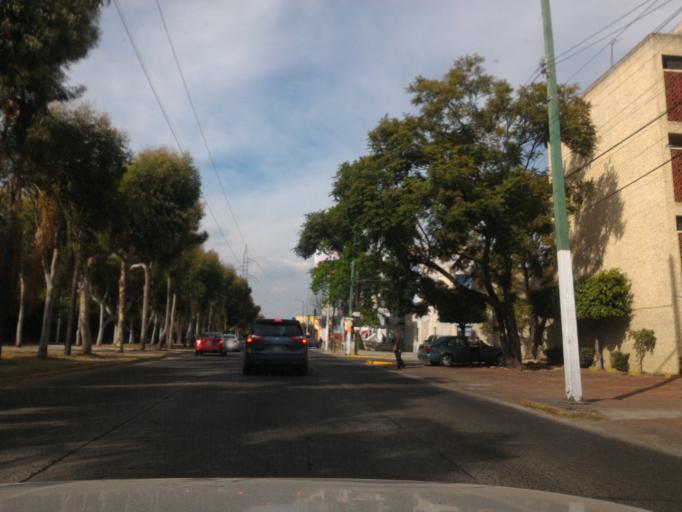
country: MX
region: Jalisco
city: Zapopan2
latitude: 20.6968
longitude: -103.4157
